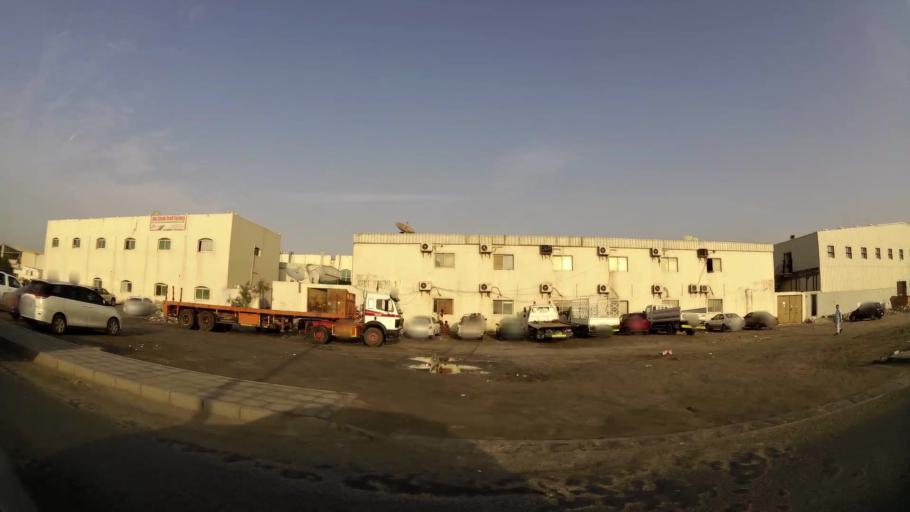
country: AE
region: Abu Dhabi
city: Abu Dhabi
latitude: 24.3580
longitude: 54.5020
